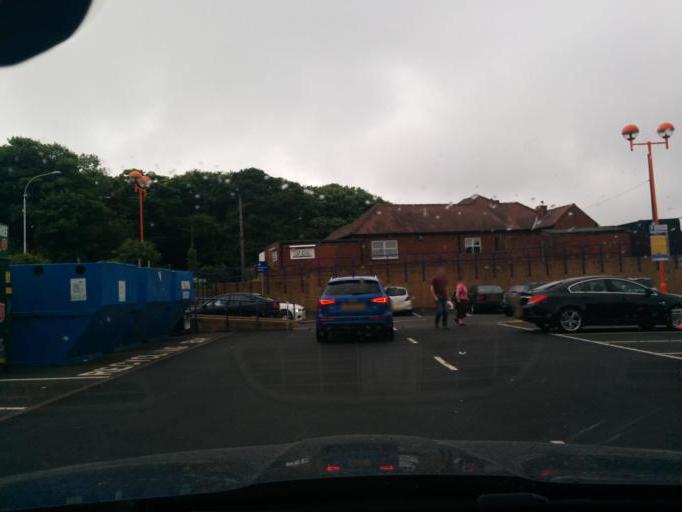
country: GB
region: England
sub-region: Northumberland
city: Cramlington
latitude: 55.0864
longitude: -1.5859
